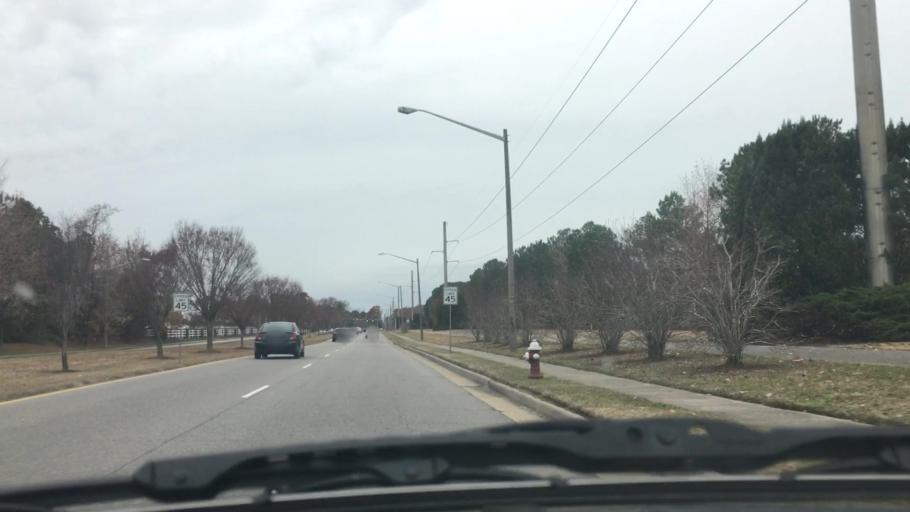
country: US
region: Virginia
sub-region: City of Virginia Beach
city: Virginia Beach
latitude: 36.8102
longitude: -76.1215
